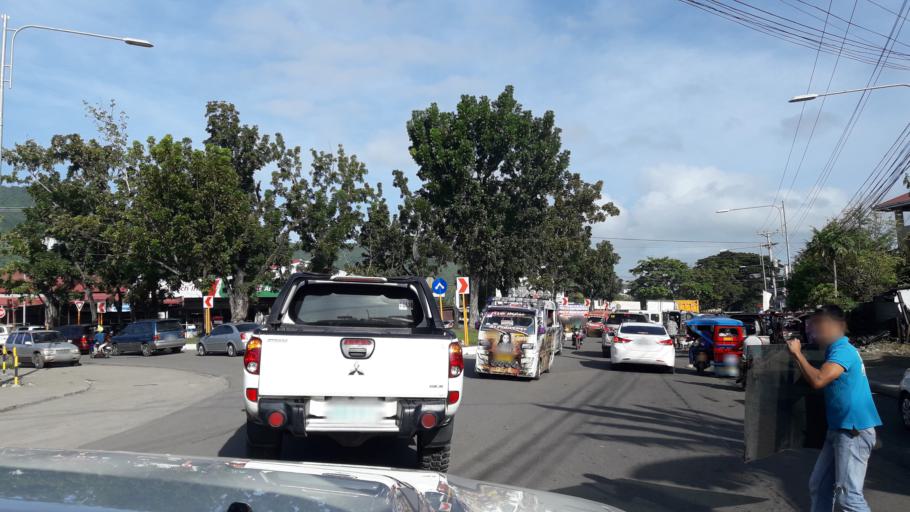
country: PH
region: Eastern Visayas
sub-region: Province of Leyte
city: Panalanoy
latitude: 11.2171
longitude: 124.9945
